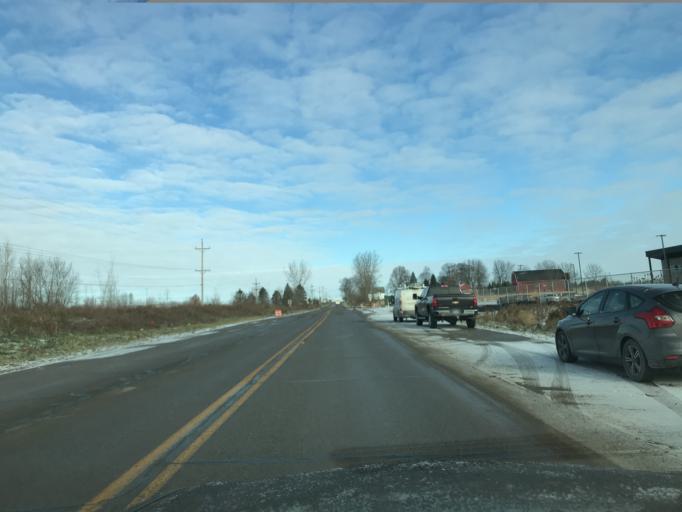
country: US
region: Michigan
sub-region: Eaton County
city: Dimondale
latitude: 42.6791
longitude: -84.6423
